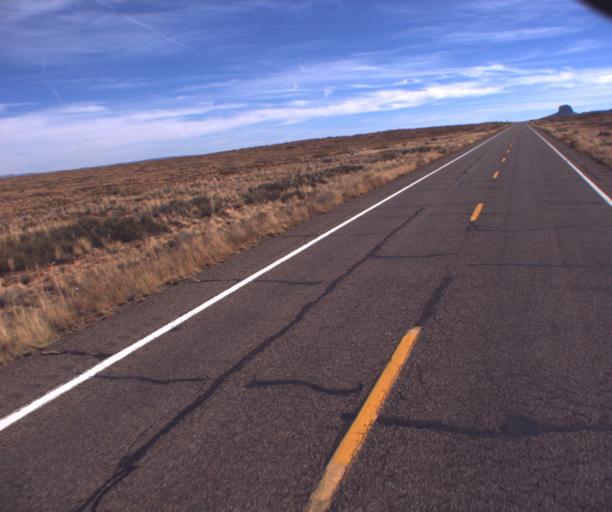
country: US
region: Arizona
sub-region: Coconino County
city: Kaibito
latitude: 36.6122
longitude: -111.0254
